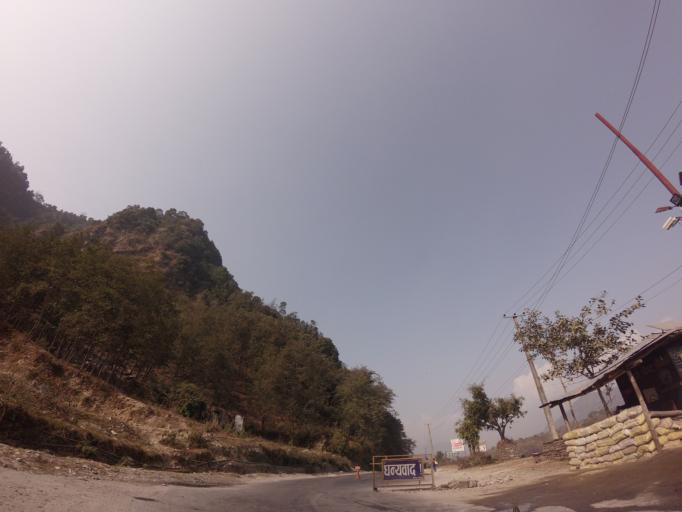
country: NP
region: Western Region
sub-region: Gandaki Zone
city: Pokhara
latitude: 28.2489
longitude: 83.9737
